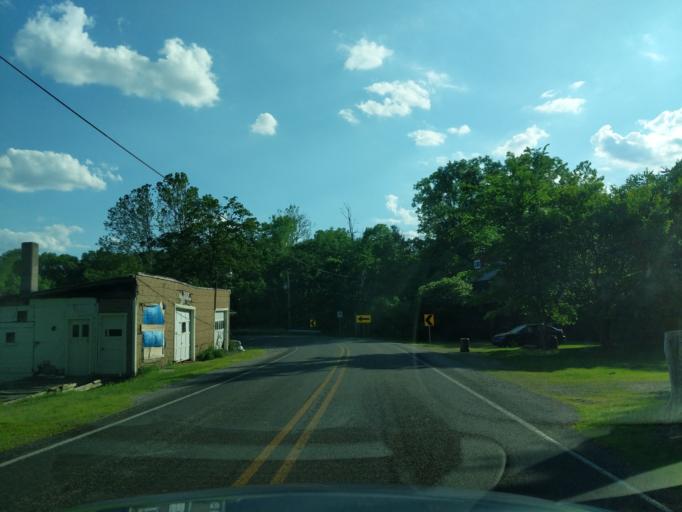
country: US
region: Indiana
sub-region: Kosciusko County
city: North Webster
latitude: 41.3096
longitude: -85.6440
